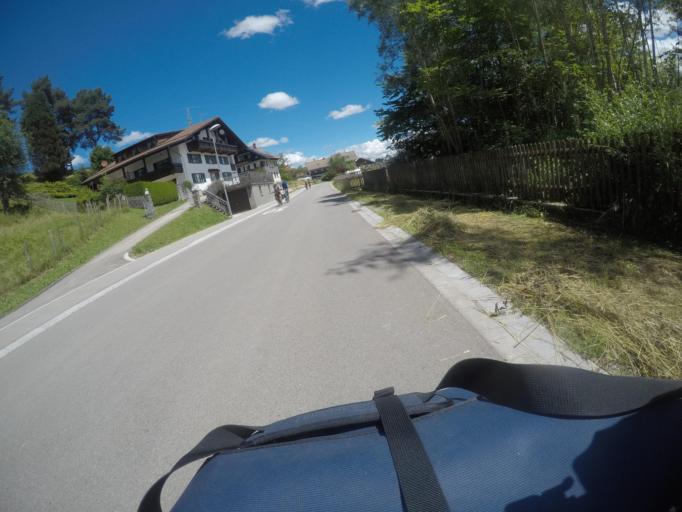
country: DE
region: Bavaria
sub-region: Swabia
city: Lechbruck
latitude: 47.6922
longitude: 10.7961
